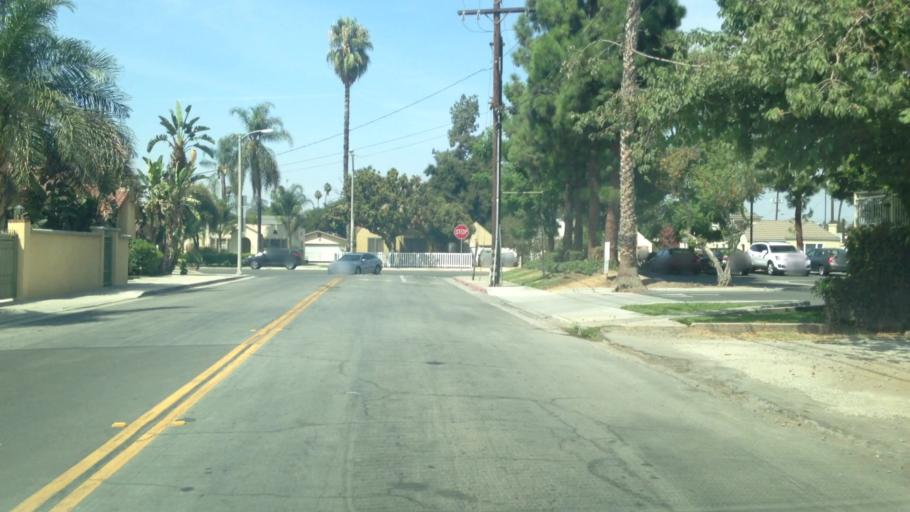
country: US
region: California
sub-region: Riverside County
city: Riverside
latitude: 33.9529
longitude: -117.3981
